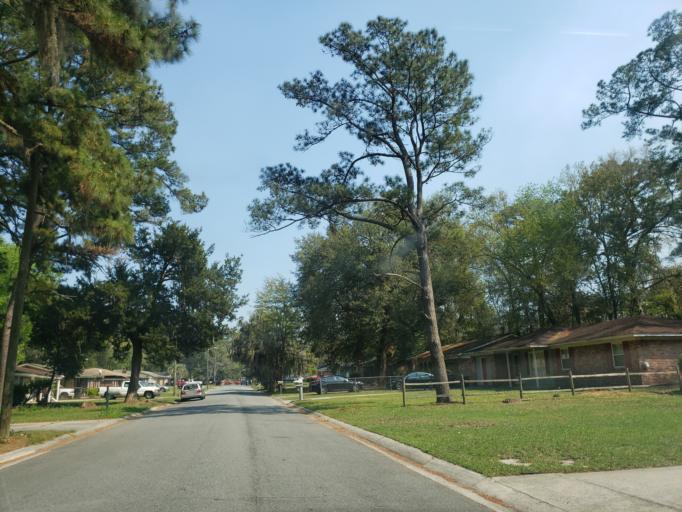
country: US
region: Georgia
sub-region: Chatham County
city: Isle of Hope
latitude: 32.0072
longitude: -81.0738
